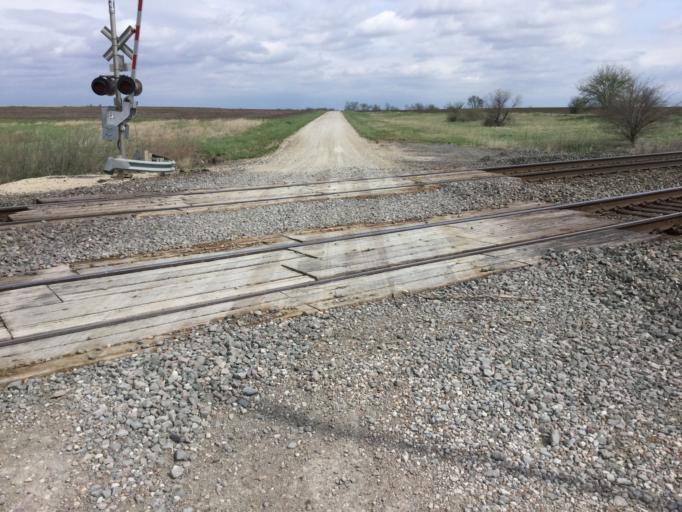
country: US
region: Kansas
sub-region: Lyon County
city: Emporia
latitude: 38.3872
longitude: -95.9505
